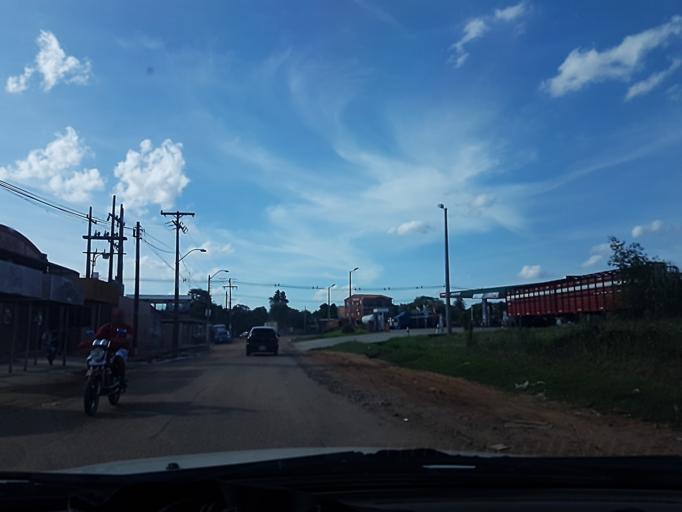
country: PY
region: Central
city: Limpio
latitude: -25.1749
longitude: -57.4824
